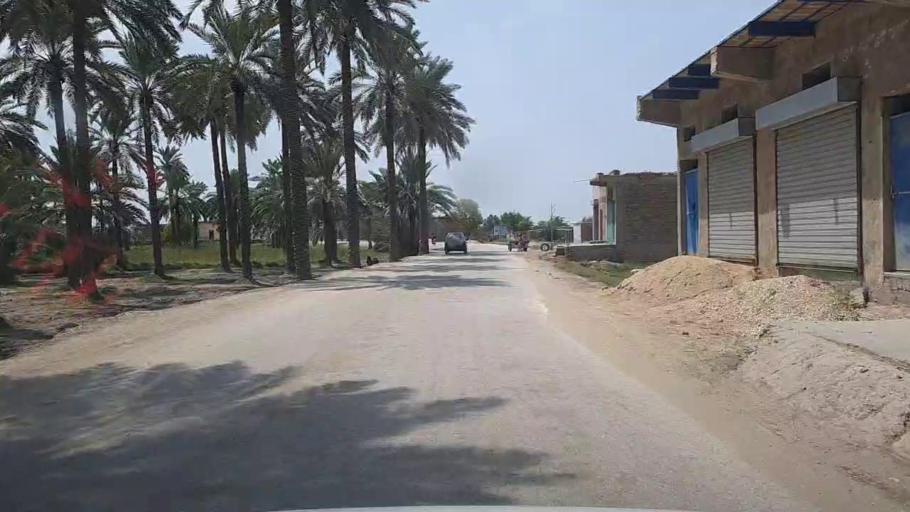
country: PK
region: Sindh
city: Pano Aqil
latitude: 27.8558
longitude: 69.1255
